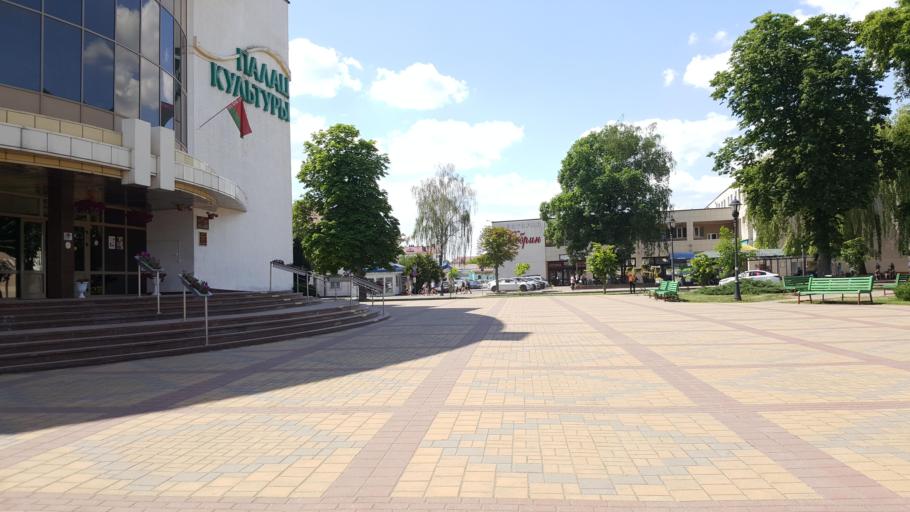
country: BY
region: Brest
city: Kobryn
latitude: 52.2107
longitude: 24.3563
